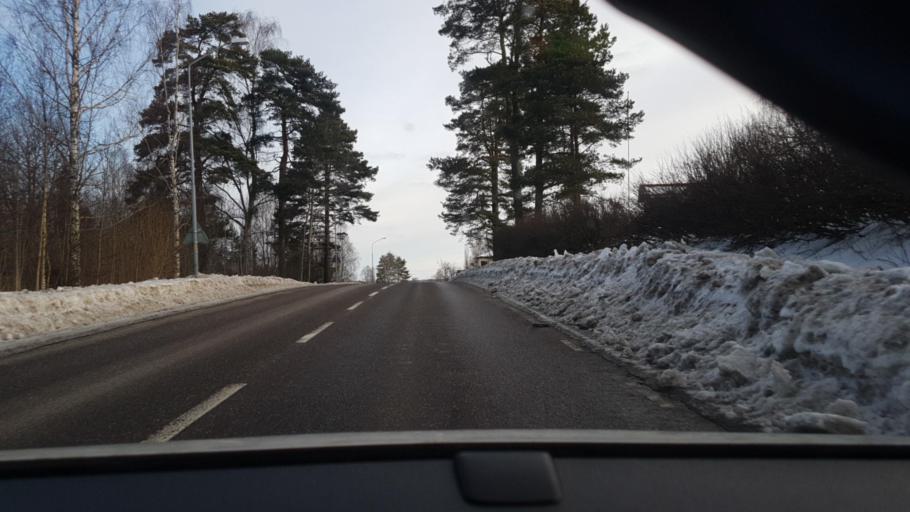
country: SE
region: Vaermland
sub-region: Eda Kommun
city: Amotfors
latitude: 59.7025
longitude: 12.1473
